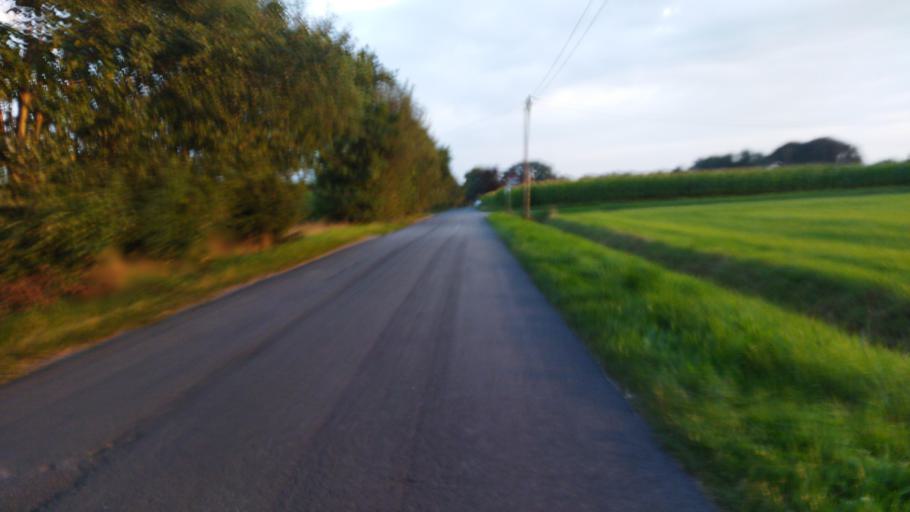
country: DE
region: Lower Saxony
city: Bad Iburg
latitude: 52.1261
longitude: 8.0575
